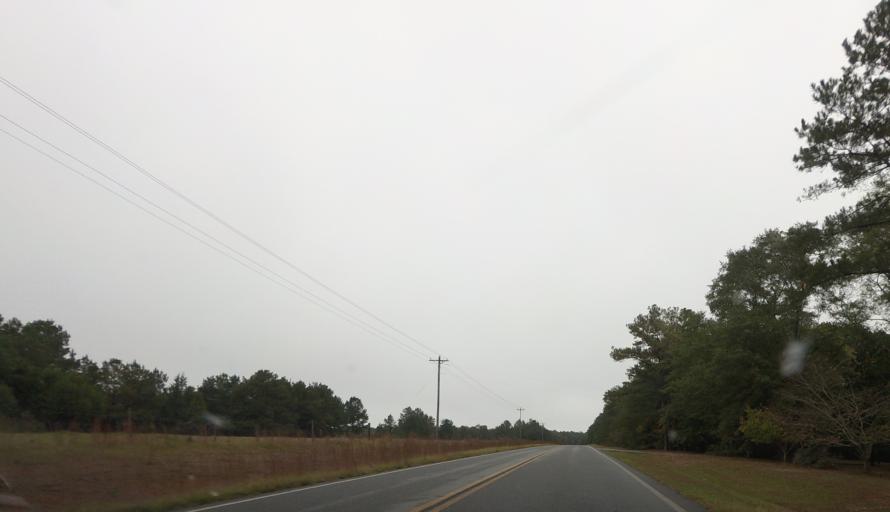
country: US
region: Georgia
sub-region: Marion County
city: Buena Vista
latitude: 32.3866
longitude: -84.4319
